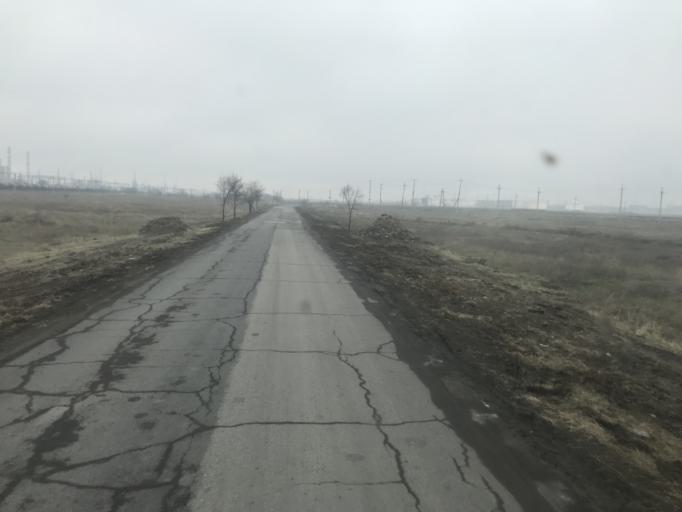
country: RU
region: Volgograd
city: Svetlyy Yar
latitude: 48.4912
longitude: 44.6594
